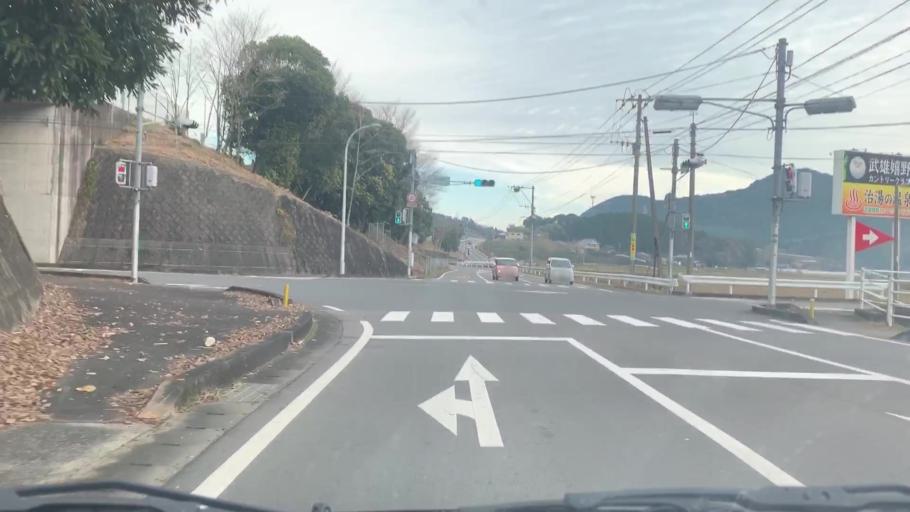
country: JP
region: Saga Prefecture
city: Ureshinomachi-shimojuku
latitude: 33.1259
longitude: 129.9819
